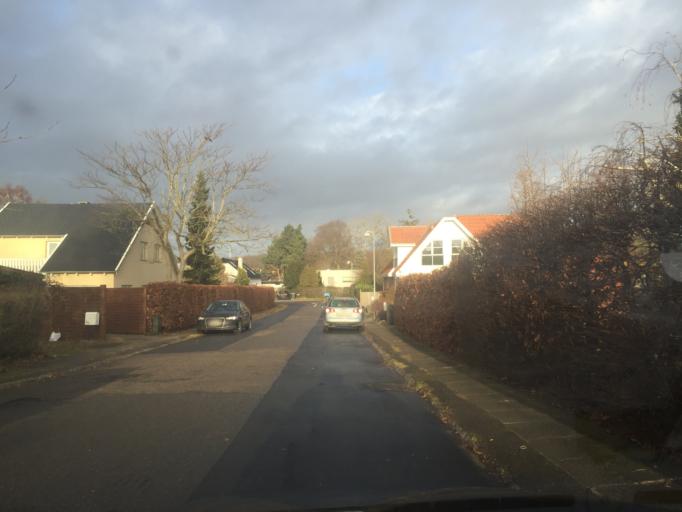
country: DK
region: Capital Region
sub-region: Fureso Kommune
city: Vaerlose
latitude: 55.7569
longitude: 12.4054
